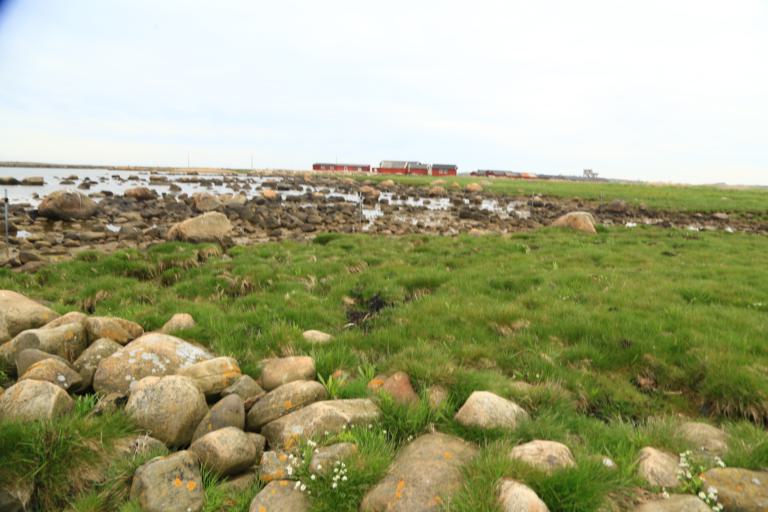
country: SE
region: Halland
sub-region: Varbergs Kommun
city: Traslovslage
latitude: 57.0267
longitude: 12.3133
